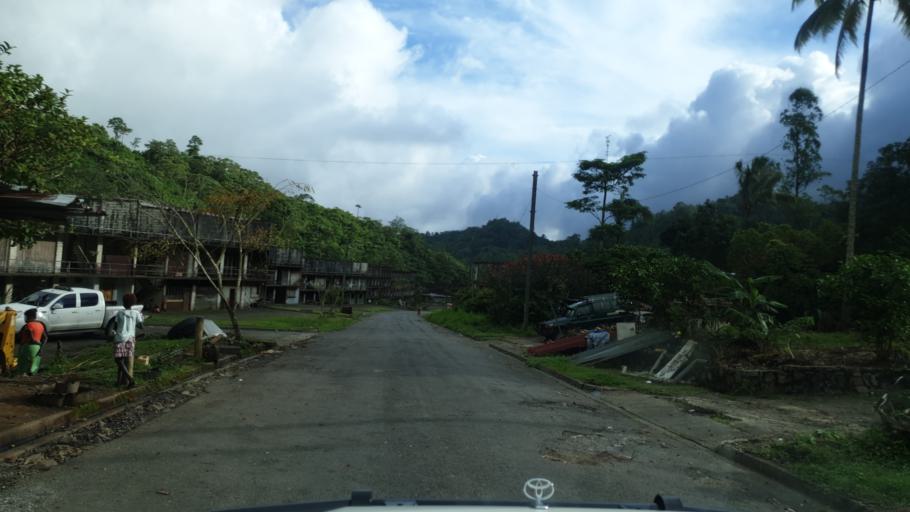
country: PG
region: Bougainville
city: Panguna
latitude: -6.3020
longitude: 155.4917
